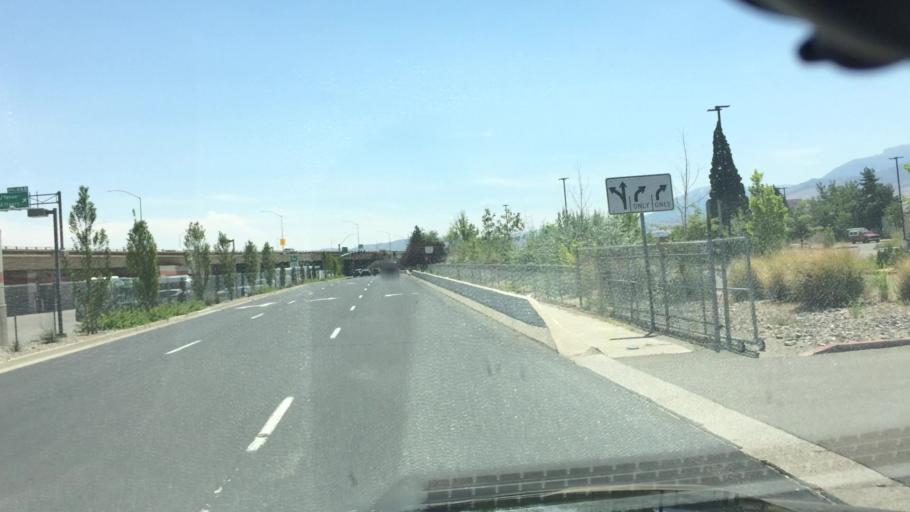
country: US
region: Nevada
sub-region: Washoe County
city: Sparks
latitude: 39.5081
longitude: -119.7809
